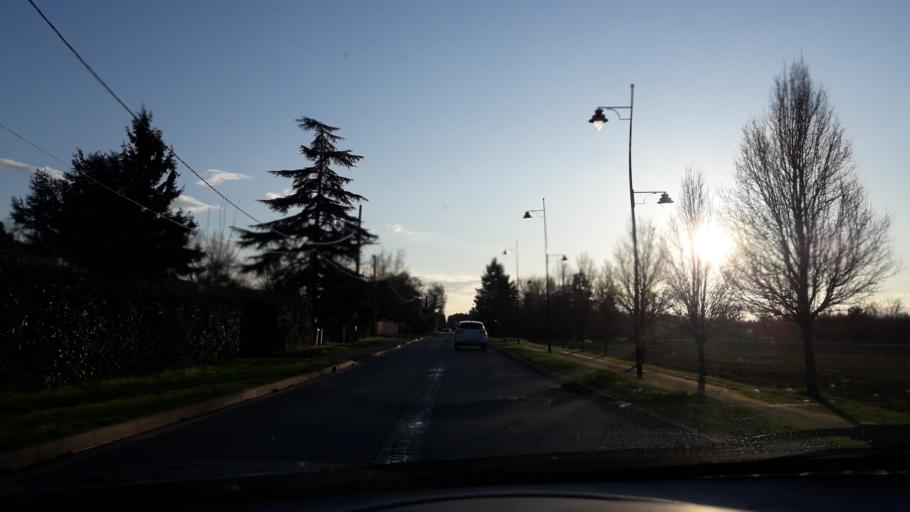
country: FR
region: Midi-Pyrenees
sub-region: Departement de la Haute-Garonne
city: Levignac
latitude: 43.6707
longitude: 1.2000
